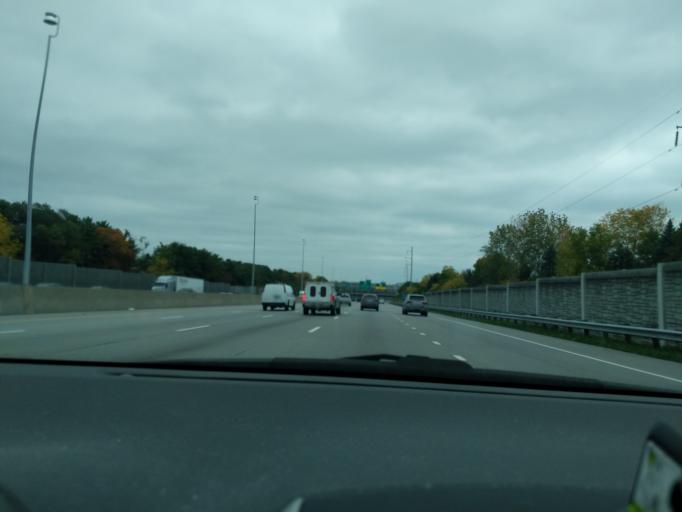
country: US
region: Ohio
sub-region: Franklin County
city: Worthington
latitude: 40.1104
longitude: -83.0500
